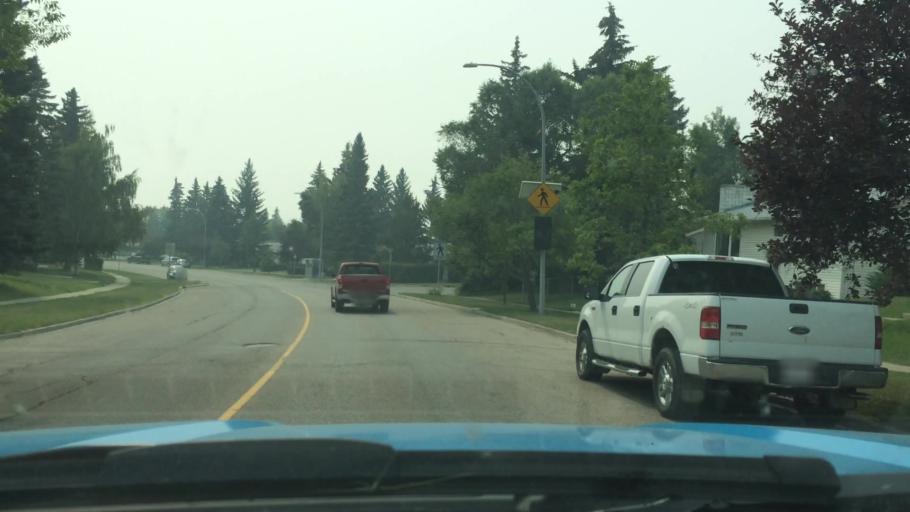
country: CA
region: Alberta
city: Calgary
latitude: 51.1016
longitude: -114.1292
